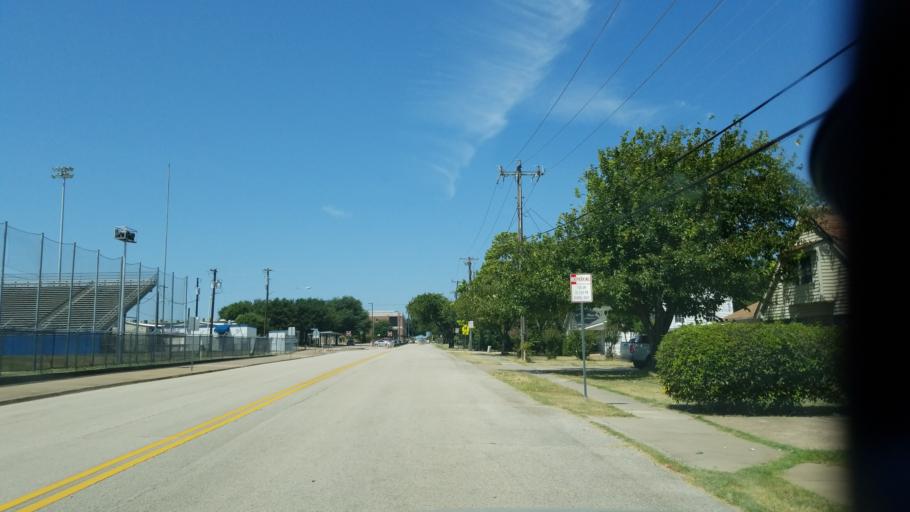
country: US
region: Texas
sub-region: Dallas County
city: Duncanville
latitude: 32.6510
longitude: -96.9034
